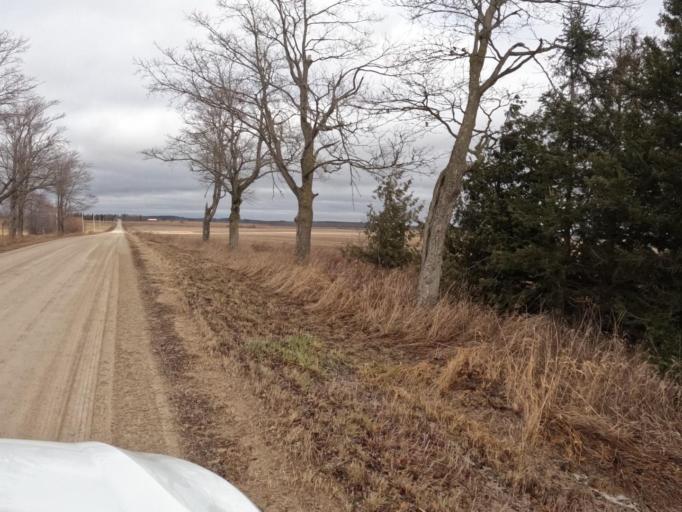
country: CA
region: Ontario
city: Shelburne
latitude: 43.9976
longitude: -80.4089
